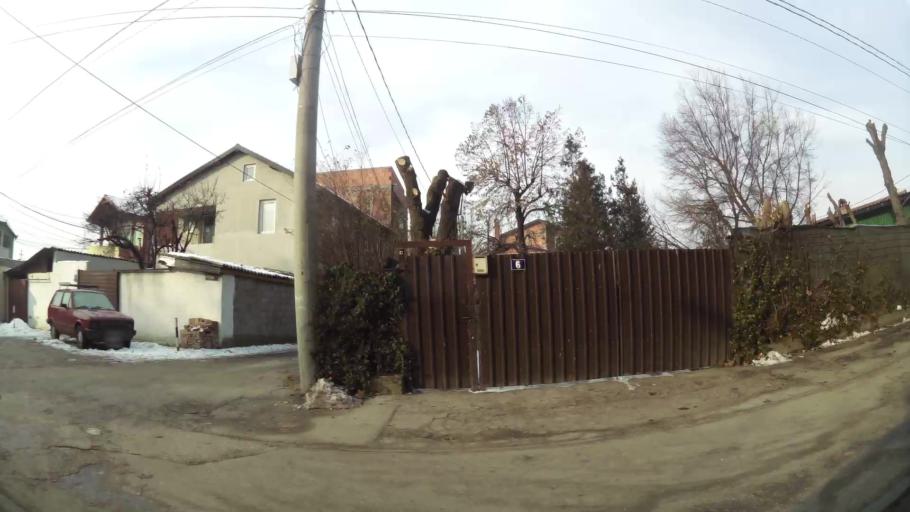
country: MK
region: Cair
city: Cair
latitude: 42.0198
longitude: 21.4308
